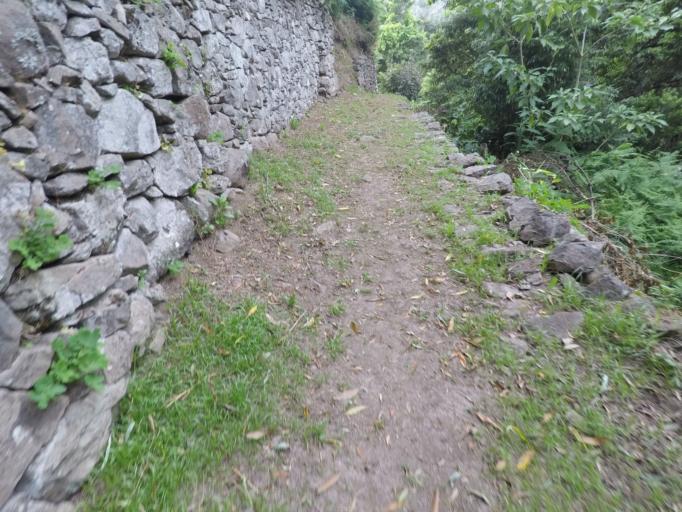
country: PT
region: Madeira
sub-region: Sao Vicente
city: Sao Vicente
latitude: 32.8159
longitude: -16.9677
